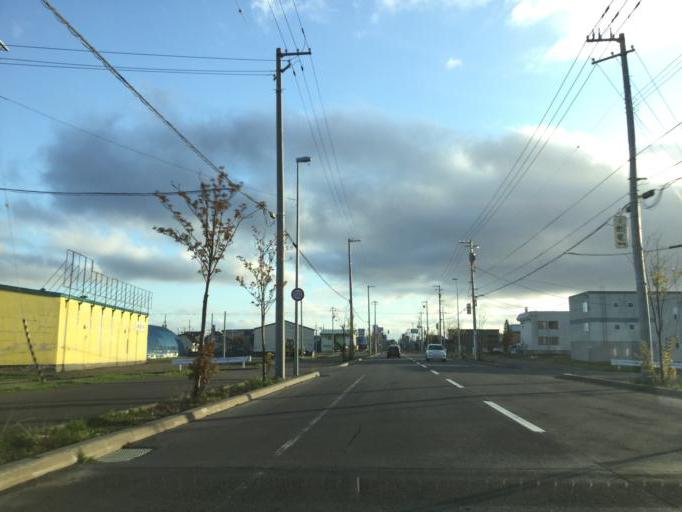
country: JP
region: Hokkaido
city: Iwamizawa
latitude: 43.1935
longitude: 141.7469
